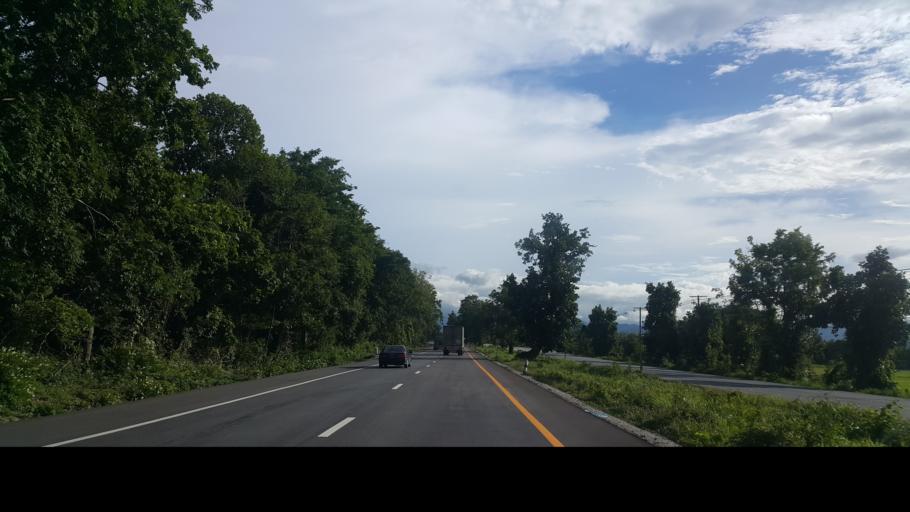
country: TH
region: Tak
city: Ban Tak
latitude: 17.1277
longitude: 99.1004
